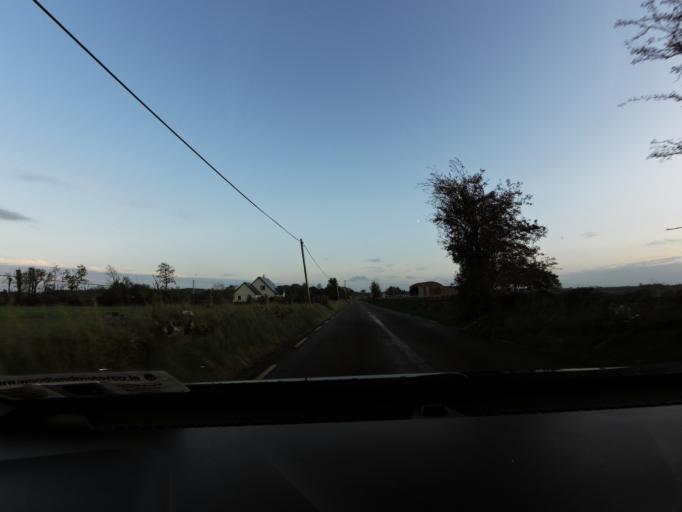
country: IE
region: Connaught
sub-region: County Galway
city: Tuam
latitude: 53.5208
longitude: -8.6191
